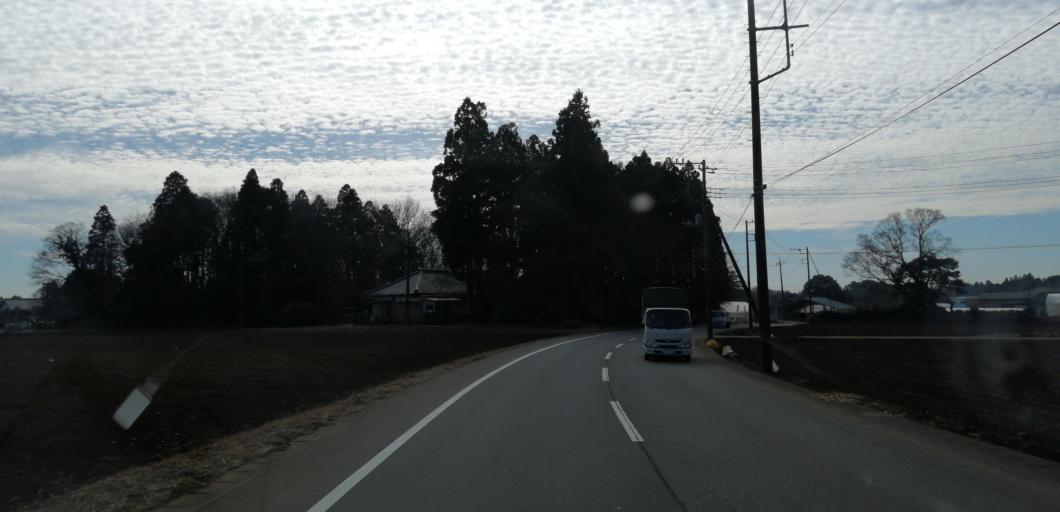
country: JP
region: Chiba
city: Narita
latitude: 35.7670
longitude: 140.3632
